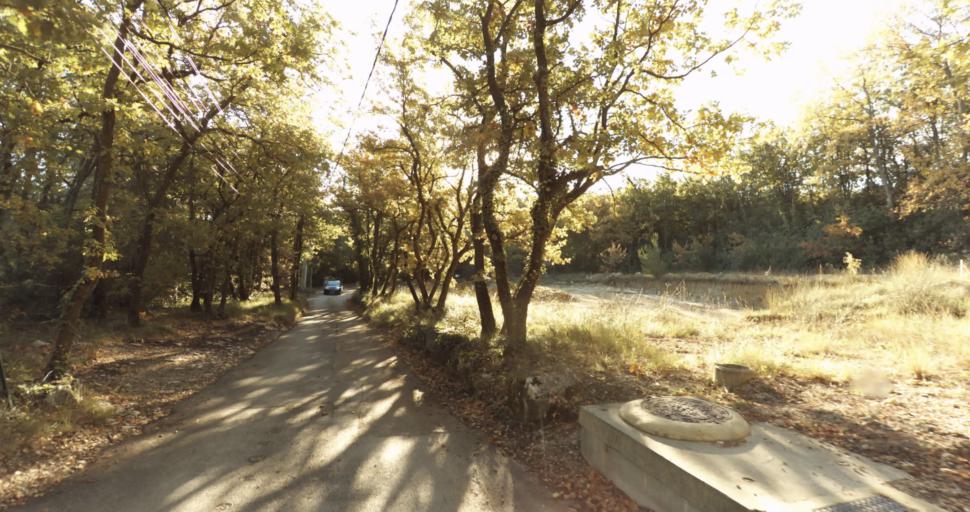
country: FR
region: Provence-Alpes-Cote d'Azur
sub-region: Departement des Bouches-du-Rhone
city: Venelles
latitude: 43.6098
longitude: 5.4789
